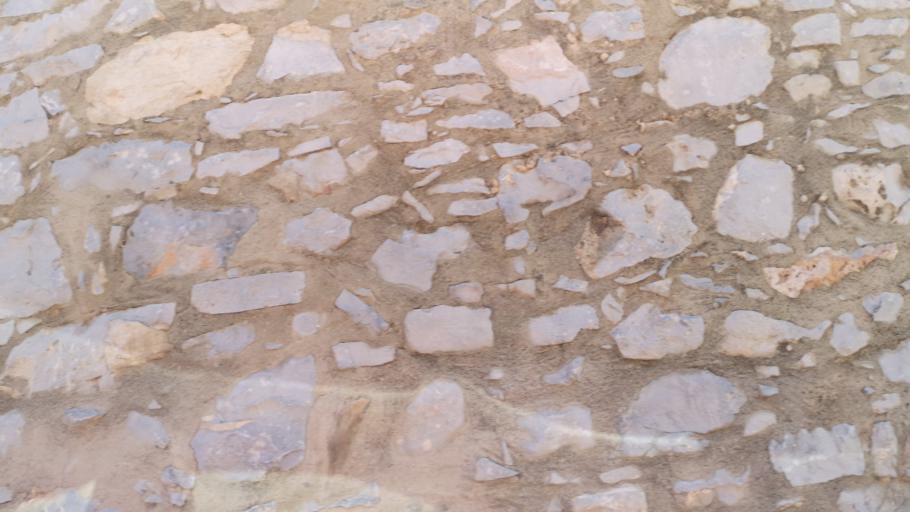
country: GR
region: Crete
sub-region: Nomos Lasithiou
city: Neapoli
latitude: 35.2591
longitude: 25.6505
